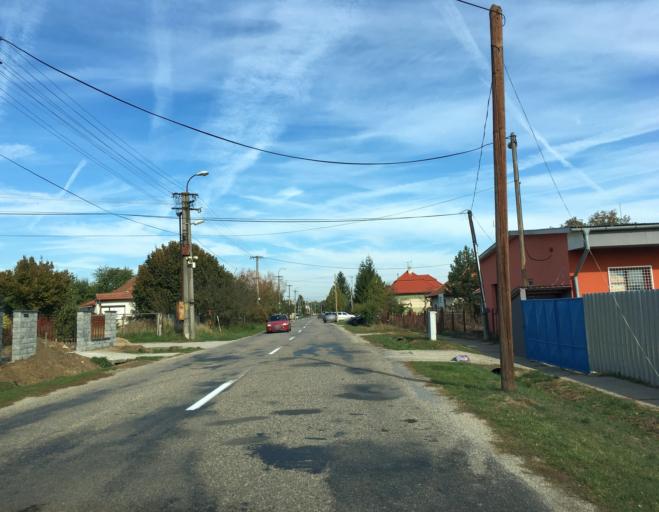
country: SK
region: Nitriansky
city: Svodin
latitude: 48.0088
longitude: 18.4142
